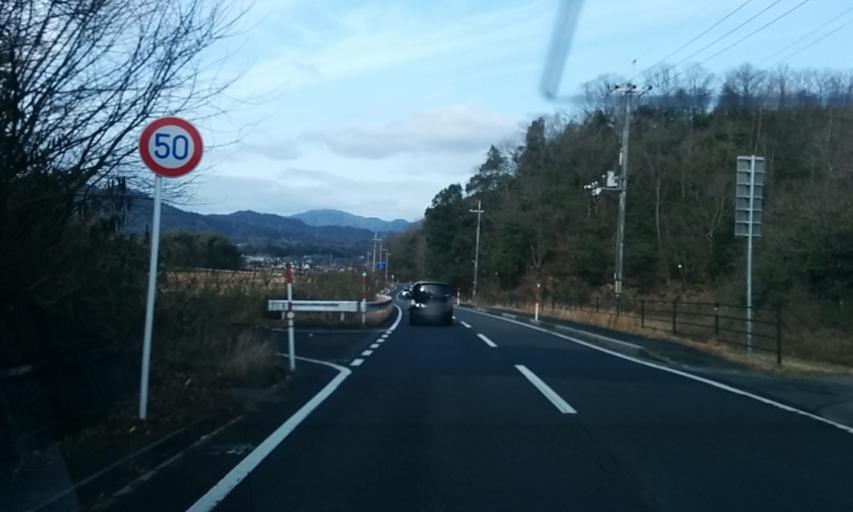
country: JP
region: Kyoto
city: Miyazu
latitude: 35.5832
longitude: 135.1098
